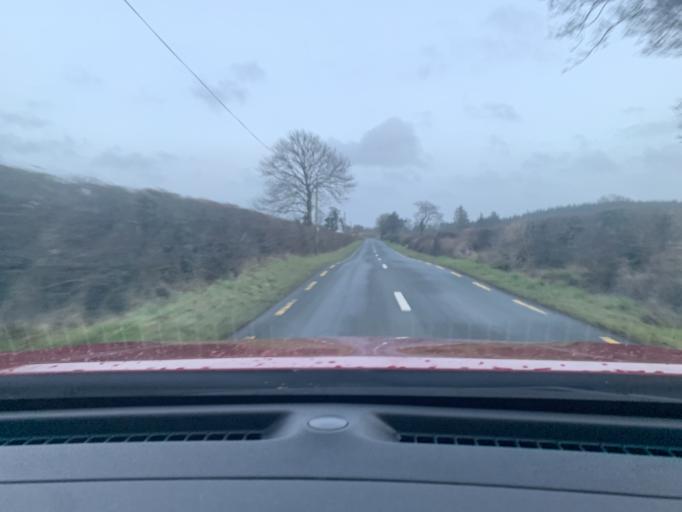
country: IE
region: Connaught
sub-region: Sligo
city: Ballymote
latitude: 54.0411
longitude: -8.4370
